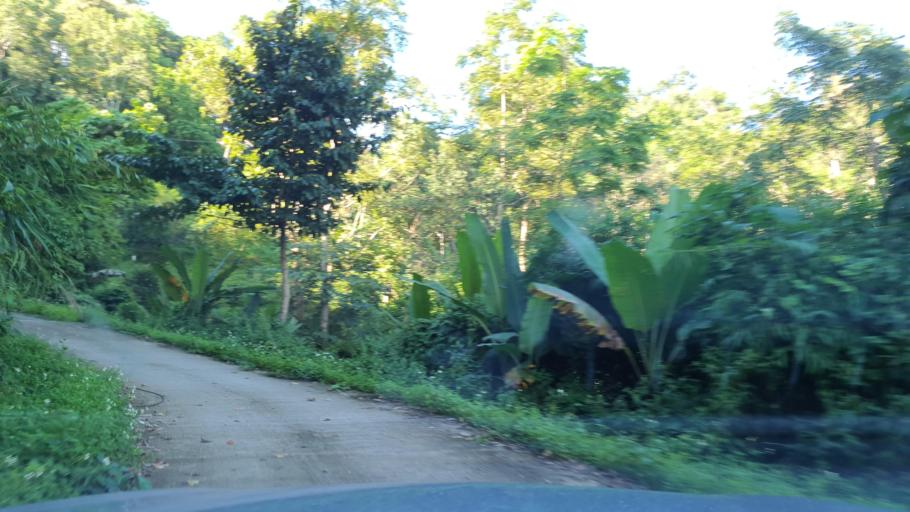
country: TH
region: Chiang Mai
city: Mae On
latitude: 18.8128
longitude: 99.3329
